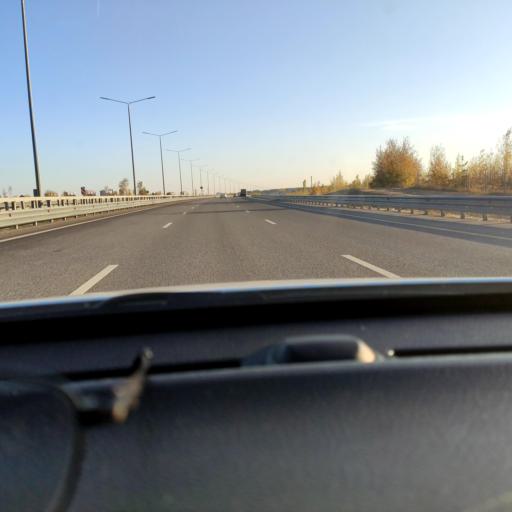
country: RU
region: Voronezj
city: Somovo
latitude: 51.7599
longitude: 39.3068
